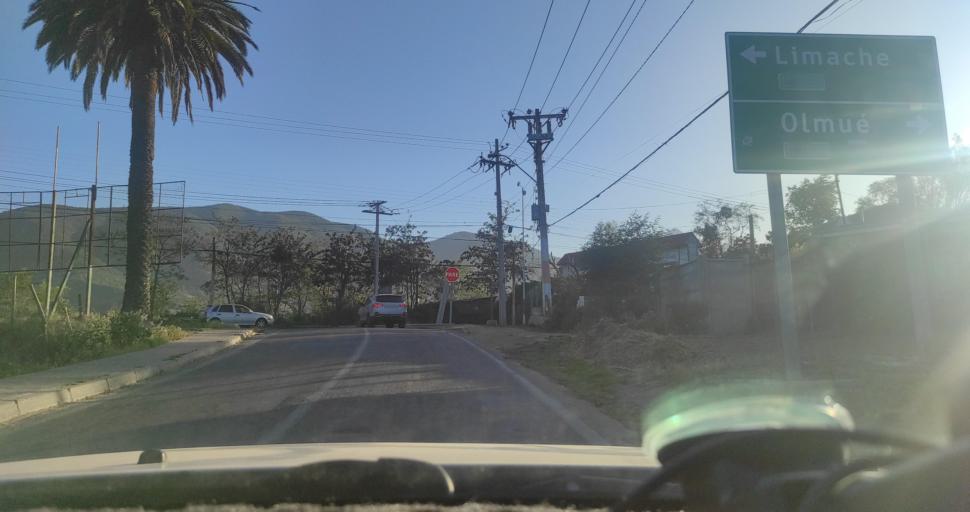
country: CL
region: Valparaiso
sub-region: Provincia de Marga Marga
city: Limache
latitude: -32.9978
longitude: -71.2206
